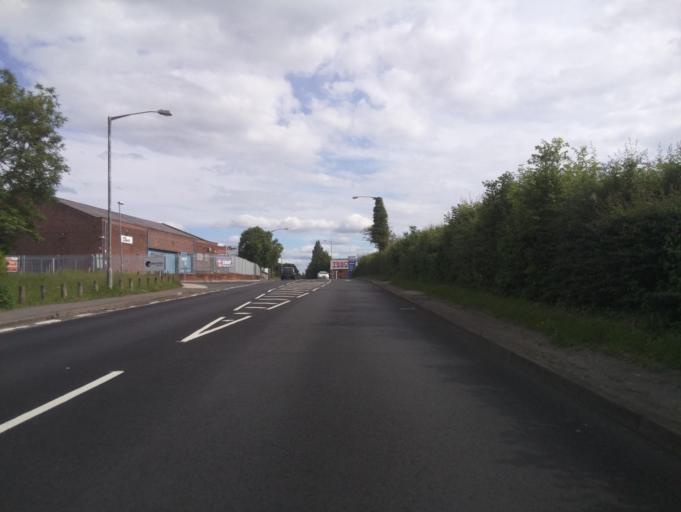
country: GB
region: England
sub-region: Worcestershire
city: Evesham
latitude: 52.1037
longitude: -1.9521
